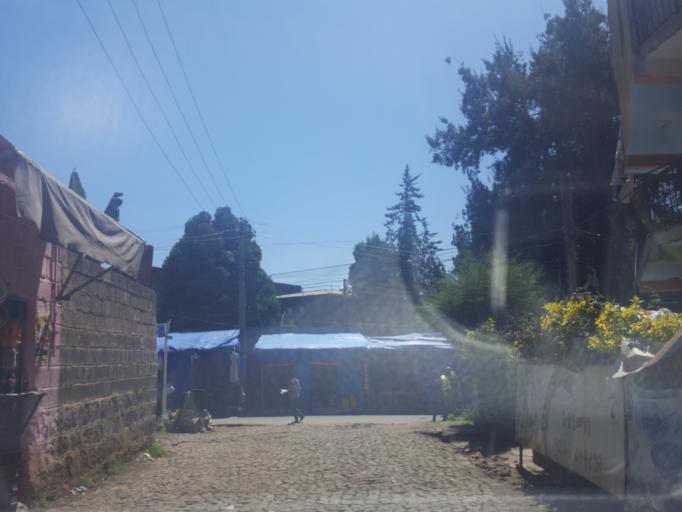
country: ET
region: Adis Abeba
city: Addis Ababa
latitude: 9.0506
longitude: 38.7608
